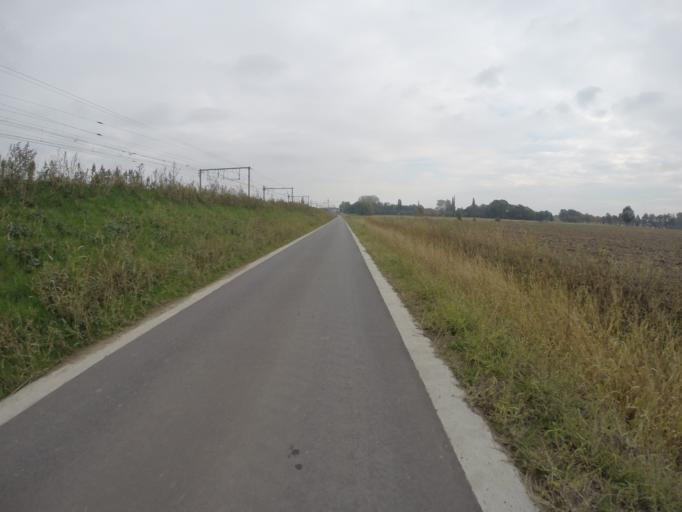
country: BE
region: Flanders
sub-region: Provincie Oost-Vlaanderen
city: Aalter
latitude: 51.0957
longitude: 3.4311
